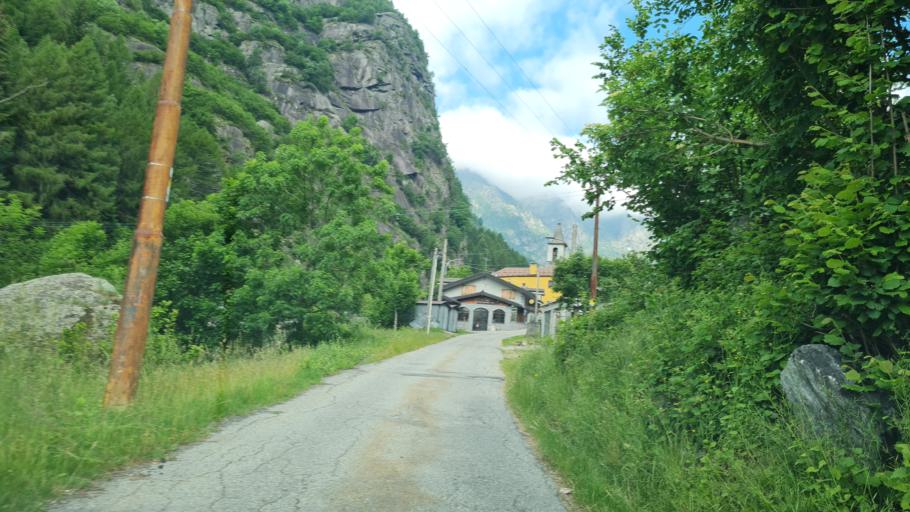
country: IT
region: Piedmont
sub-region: Provincia di Torino
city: Locana
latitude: 45.4458
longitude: 7.4127
